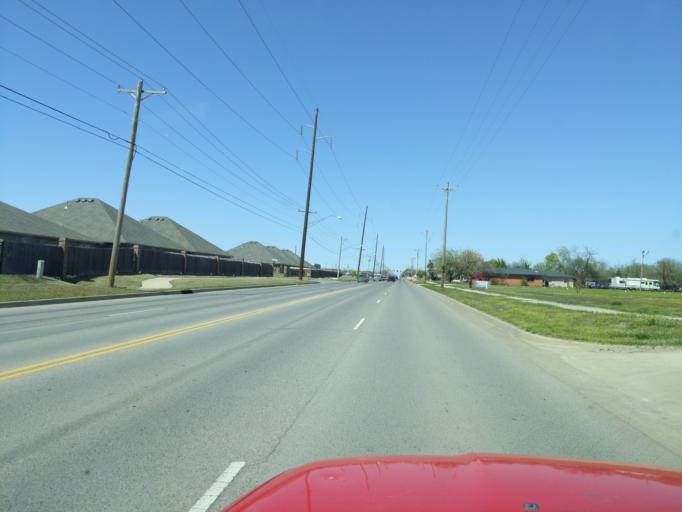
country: US
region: Oklahoma
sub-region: Cleveland County
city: Moore
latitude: 35.3303
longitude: -97.5120
